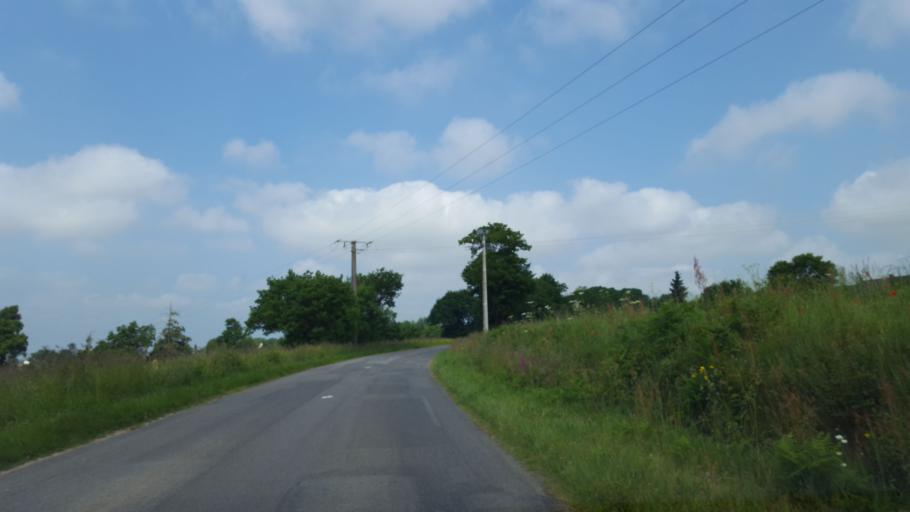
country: FR
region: Brittany
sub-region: Departement d'Ille-et-Vilaine
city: Baulon
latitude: 47.9279
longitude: -1.9323
